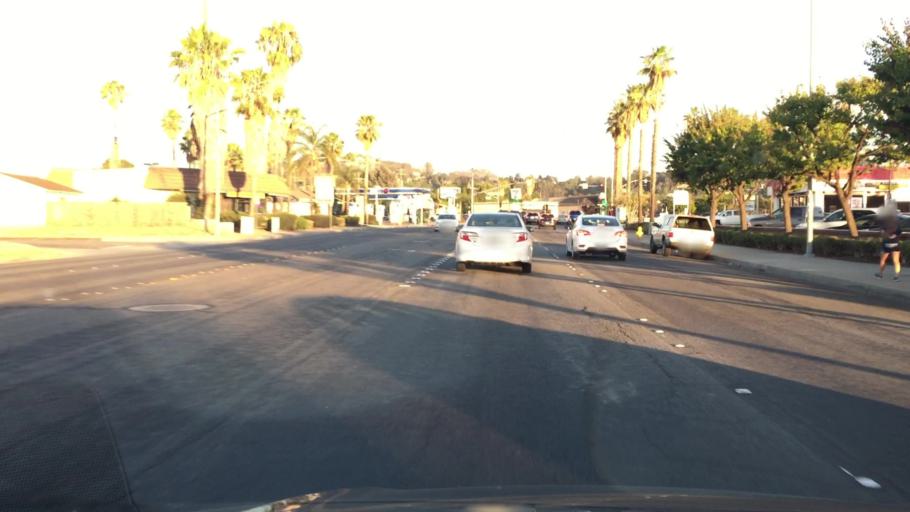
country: US
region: California
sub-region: San Diego County
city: Bostonia
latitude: 32.7888
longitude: -116.9294
